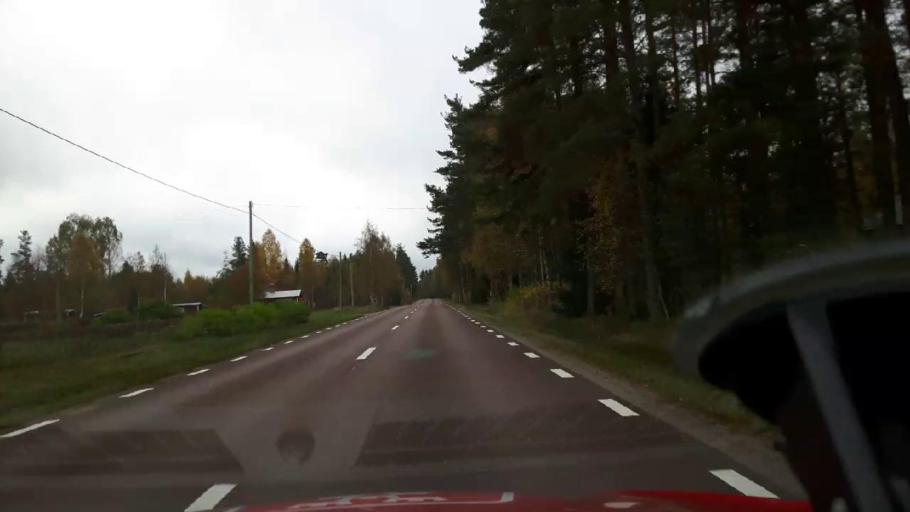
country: SE
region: Jaemtland
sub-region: Harjedalens Kommun
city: Sveg
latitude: 62.3034
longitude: 14.7710
